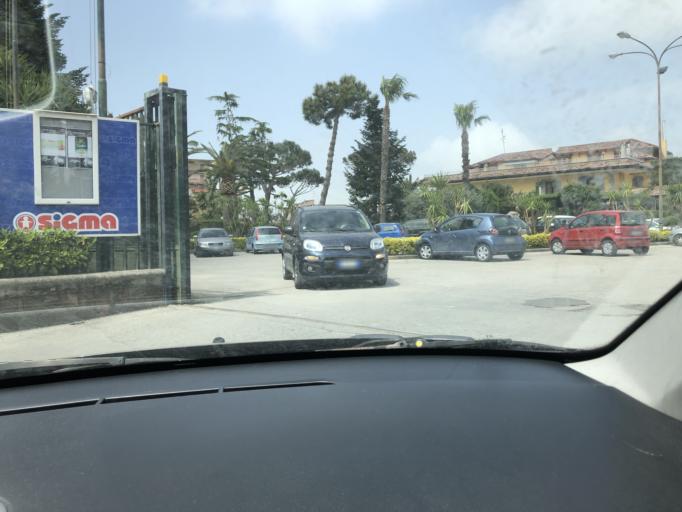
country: IT
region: Campania
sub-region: Provincia di Napoli
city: Torre Caracciolo
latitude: 40.8751
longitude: 14.1823
